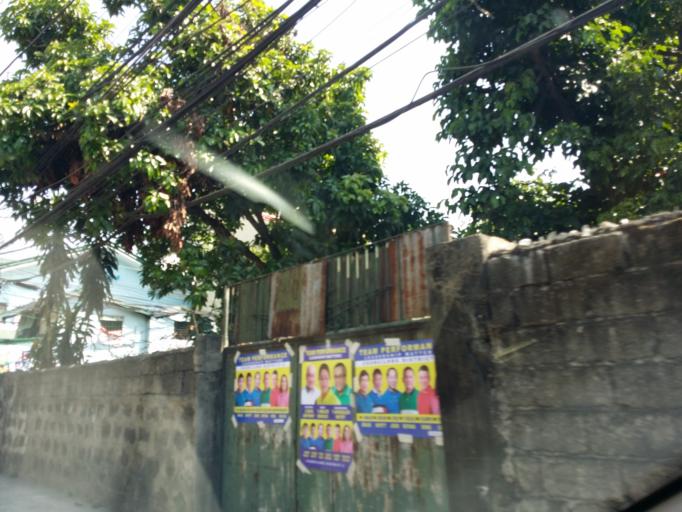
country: PH
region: Metro Manila
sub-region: San Juan
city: San Juan
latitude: 14.5859
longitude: 121.0211
